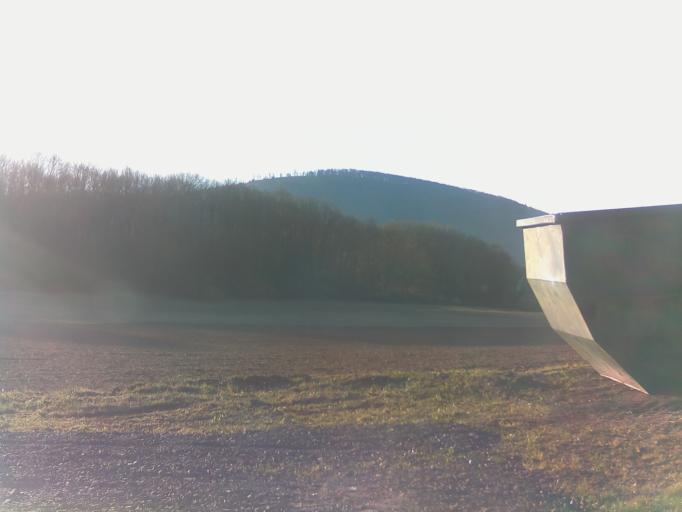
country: DE
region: Rheinland-Pfalz
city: Ruppertsecken
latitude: 49.6479
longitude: 7.8890
